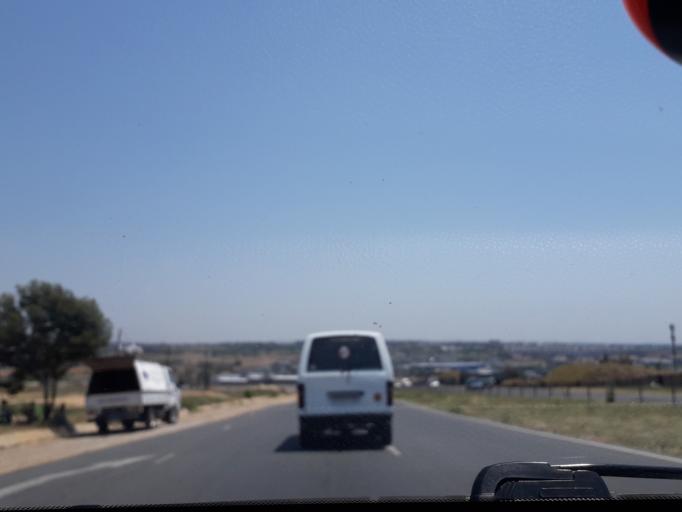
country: ZA
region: Gauteng
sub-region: City of Johannesburg Metropolitan Municipality
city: Midrand
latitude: -26.0236
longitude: 28.1167
